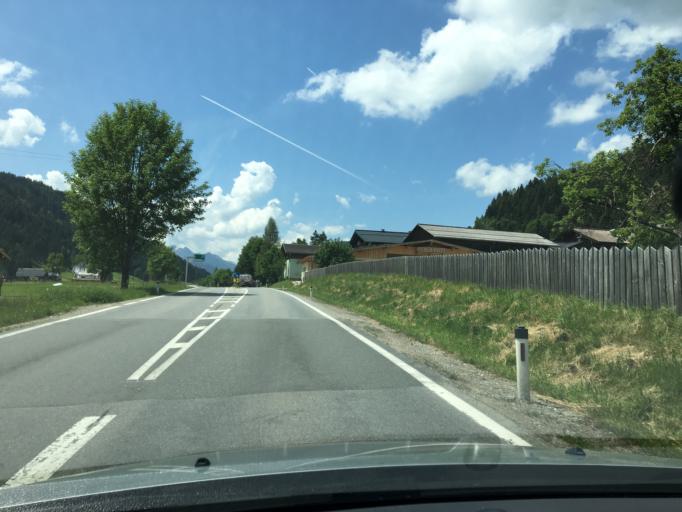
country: AT
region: Salzburg
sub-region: Politischer Bezirk Sankt Johann im Pongau
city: Flachau
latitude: 47.3592
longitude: 13.3440
